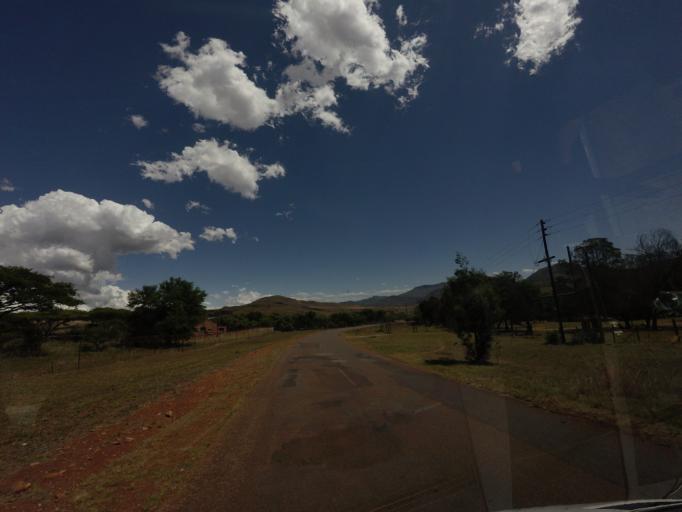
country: ZA
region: Mpumalanga
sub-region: Ehlanzeni District
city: Graksop
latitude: -24.6693
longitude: 30.8091
